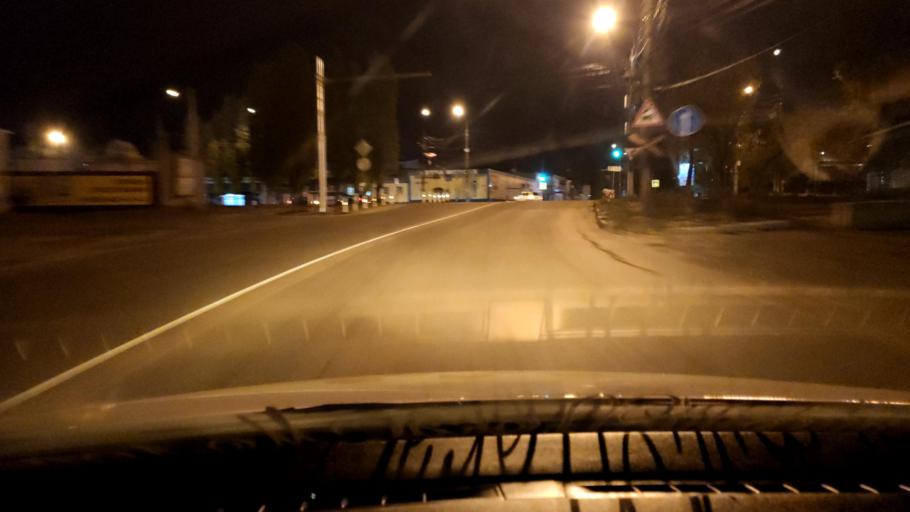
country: RU
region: Voronezj
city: Voronezh
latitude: 51.6816
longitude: 39.1648
